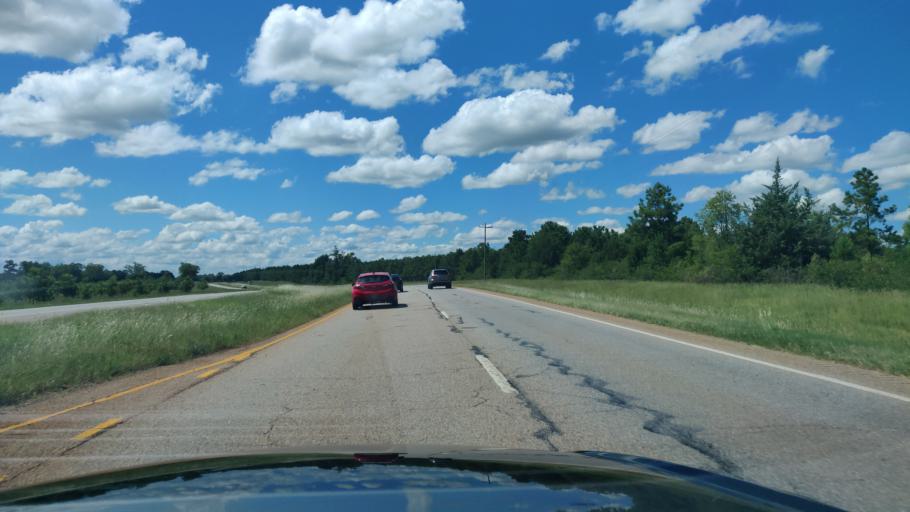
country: US
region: Georgia
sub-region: Webster County
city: Preston
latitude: 31.9430
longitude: -84.5708
